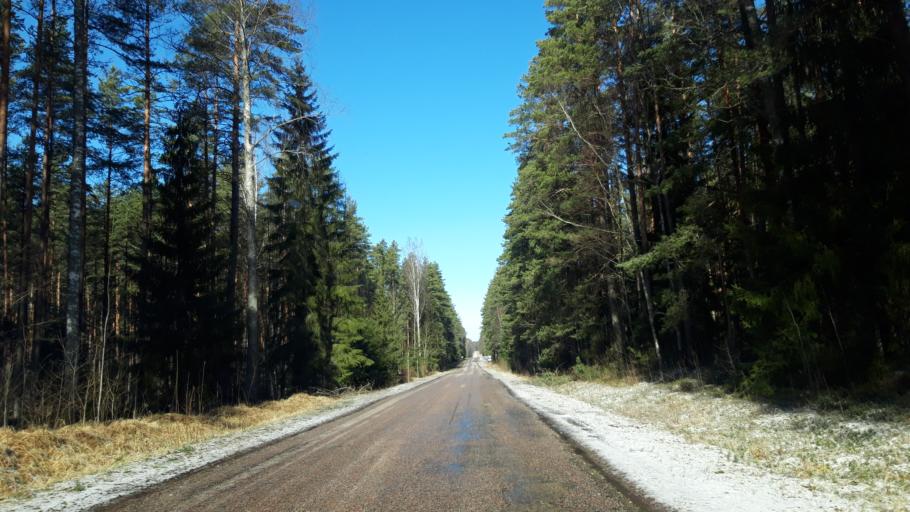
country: LV
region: Strenci
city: Strenci
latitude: 57.5968
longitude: 25.7184
